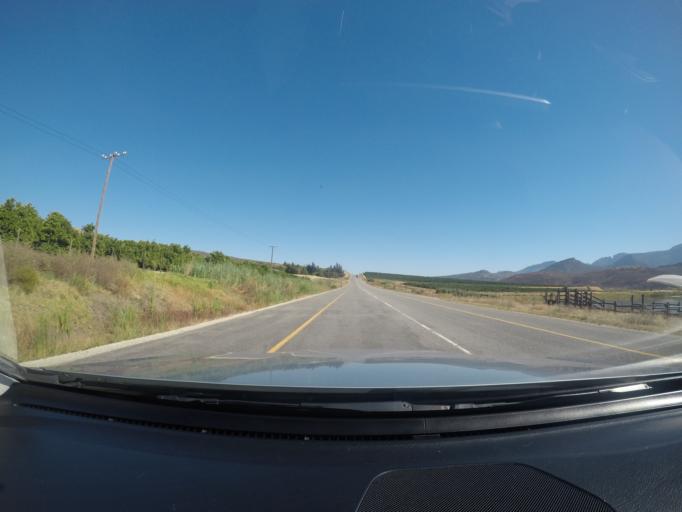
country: ZA
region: Western Cape
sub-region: West Coast District Municipality
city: Clanwilliam
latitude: -32.4772
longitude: 18.9632
